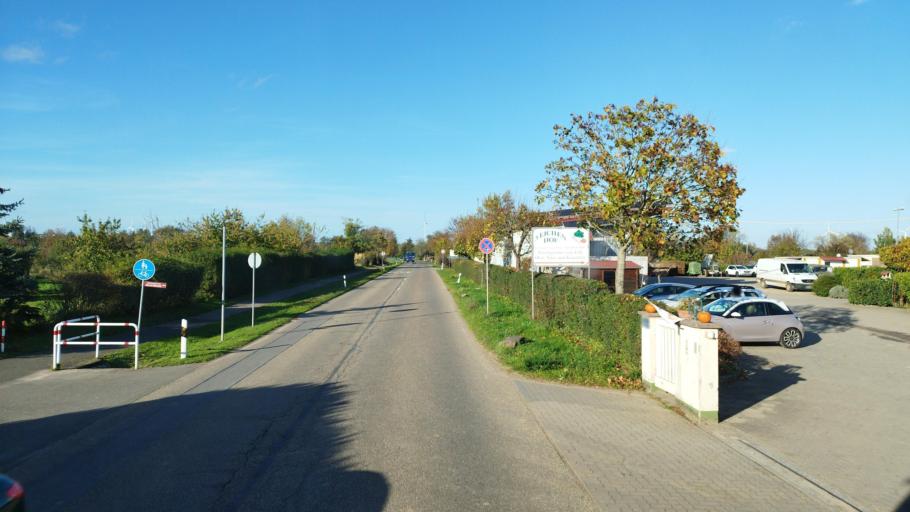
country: DE
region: Rheinland-Pfalz
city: Herxheimweyher
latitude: 49.1415
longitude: 8.2332
